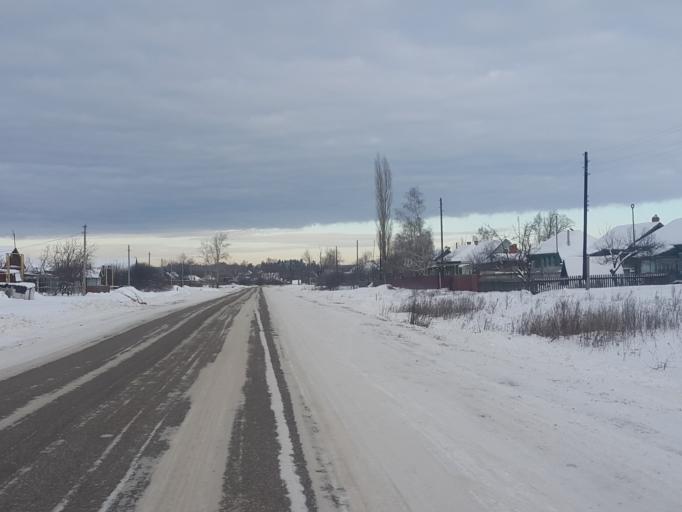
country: RU
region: Tambov
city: Platonovka
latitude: 52.8419
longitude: 41.8123
